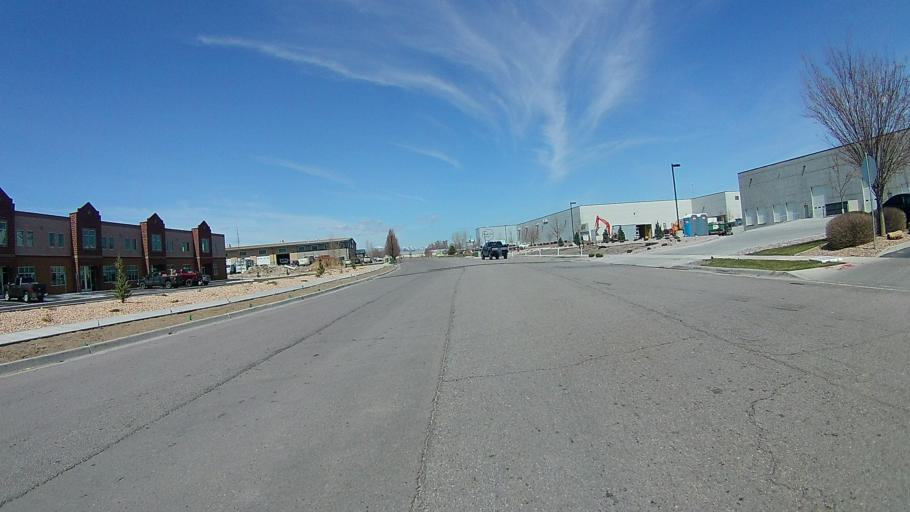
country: US
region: Utah
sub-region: Utah County
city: American Fork
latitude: 40.3611
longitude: -111.7907
